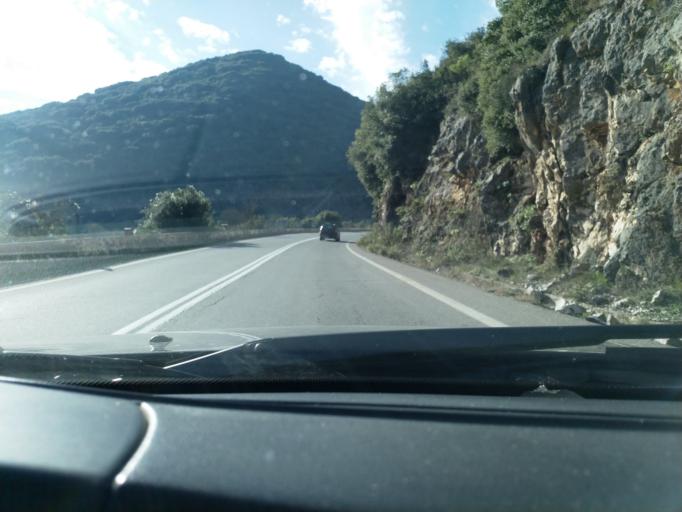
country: GR
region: Epirus
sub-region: Nomos Ioanninon
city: Agia Kyriaki
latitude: 39.5041
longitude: 20.8838
